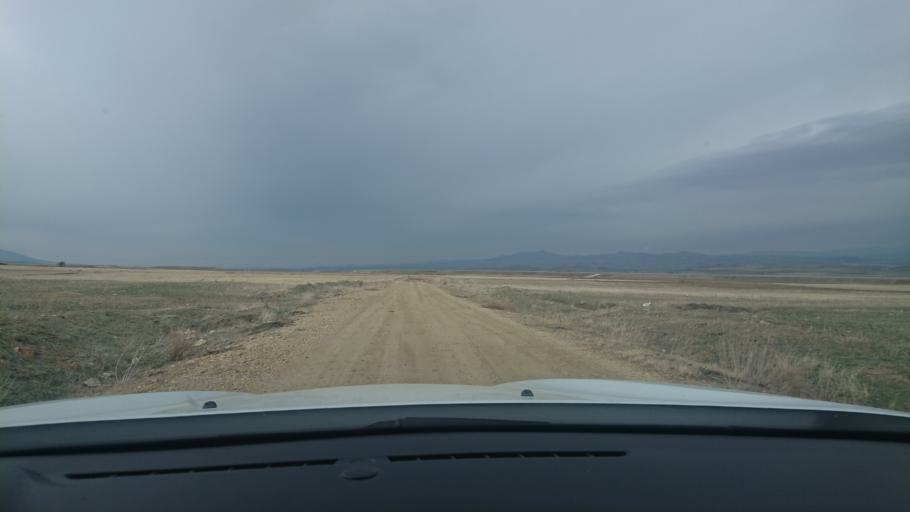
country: TR
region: Aksaray
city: Sariyahsi
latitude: 38.9803
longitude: 33.8791
